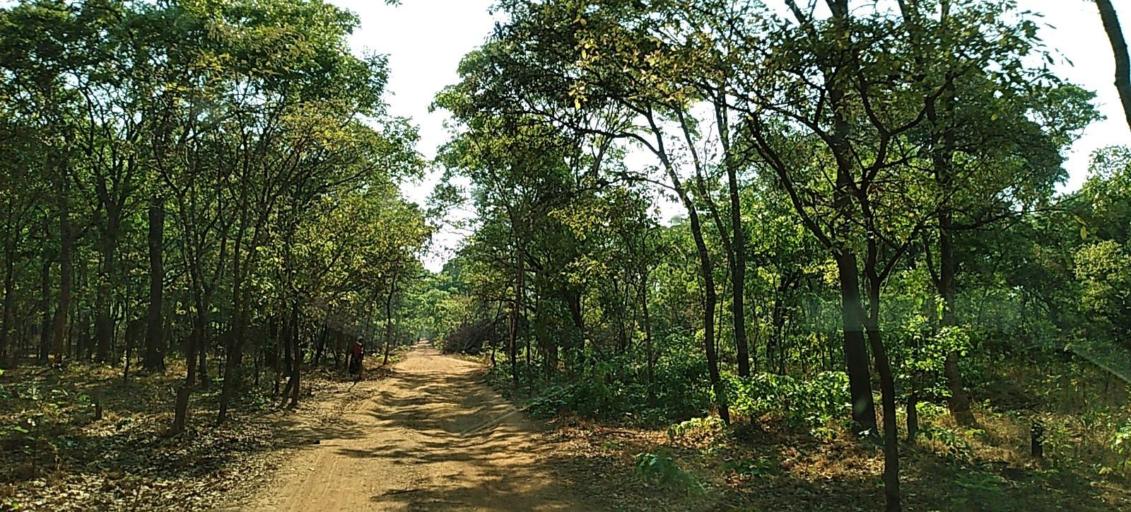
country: ZM
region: Copperbelt
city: Kalulushi
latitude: -13.0051
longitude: 27.7540
